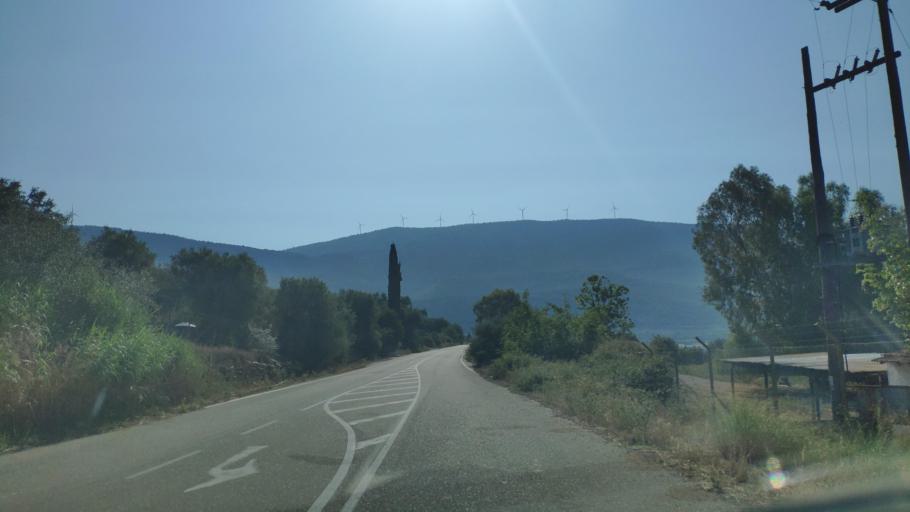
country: GR
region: West Greece
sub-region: Nomos Aitolias kai Akarnanias
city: Stanos
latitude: 38.7694
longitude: 21.1770
